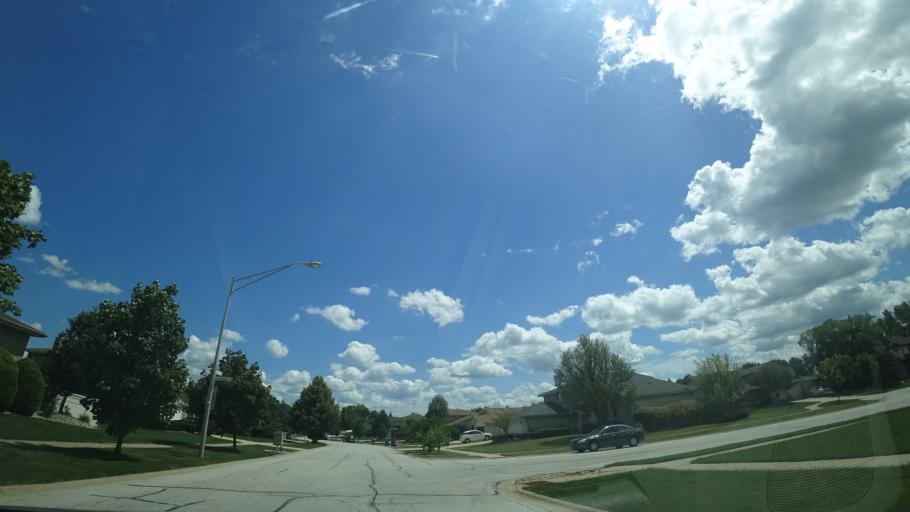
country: US
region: Illinois
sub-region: Will County
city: Homer Glen
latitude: 41.5742
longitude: -87.9052
